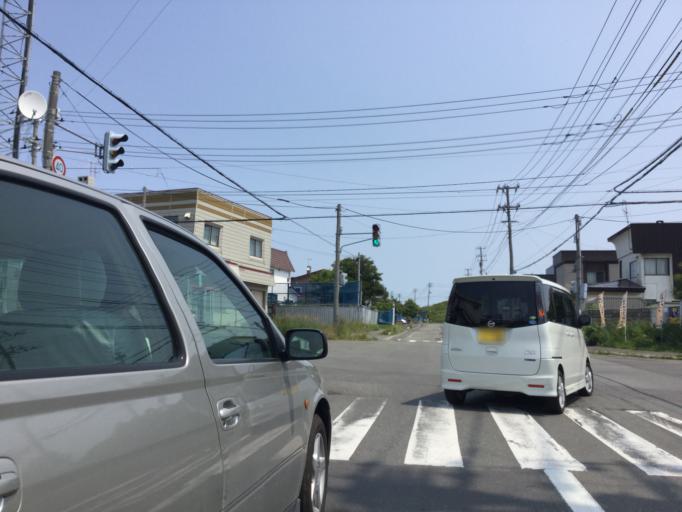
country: JP
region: Hokkaido
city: Wakkanai
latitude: 45.3875
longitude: 141.7215
